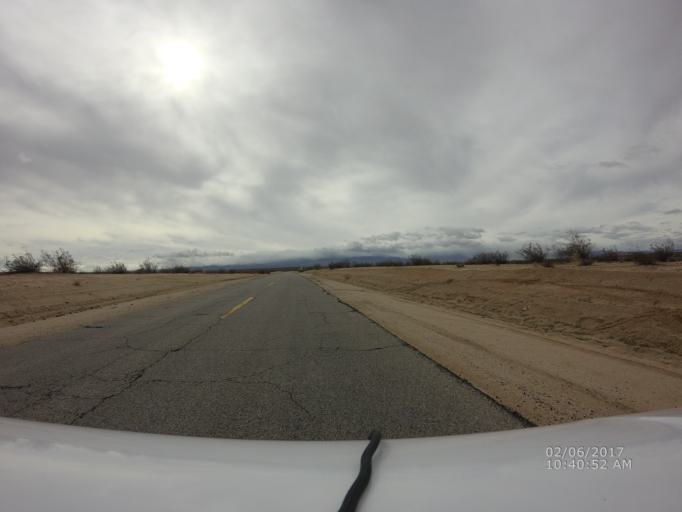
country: US
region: California
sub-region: Los Angeles County
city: Lake Los Angeles
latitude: 34.6752
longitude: -117.7026
